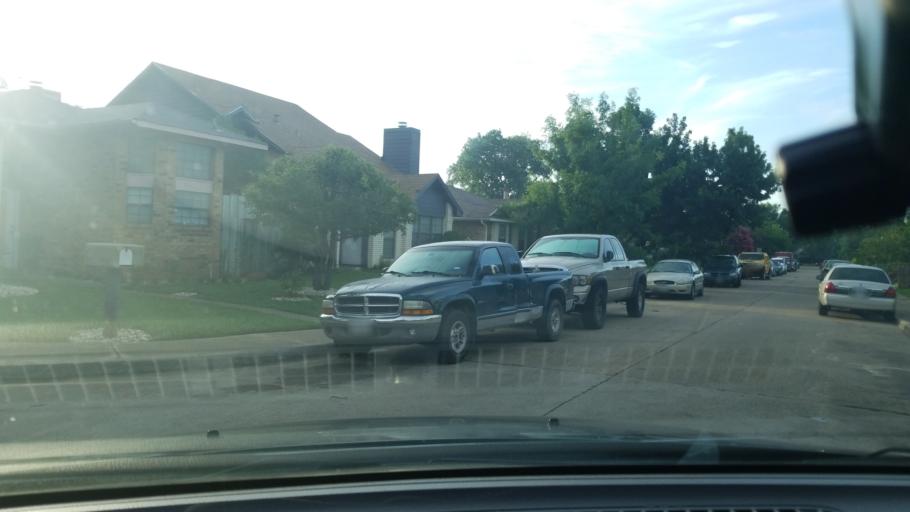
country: US
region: Texas
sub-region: Dallas County
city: Balch Springs
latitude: 32.7573
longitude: -96.6419
